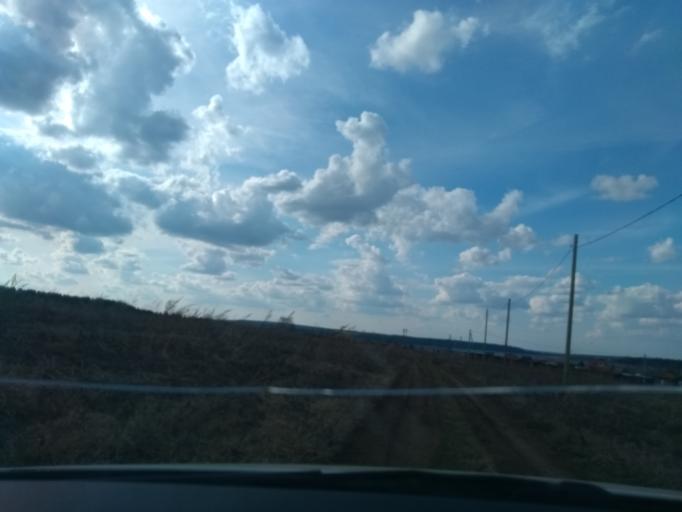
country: RU
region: Perm
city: Sylva
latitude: 57.8440
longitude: 56.7889
